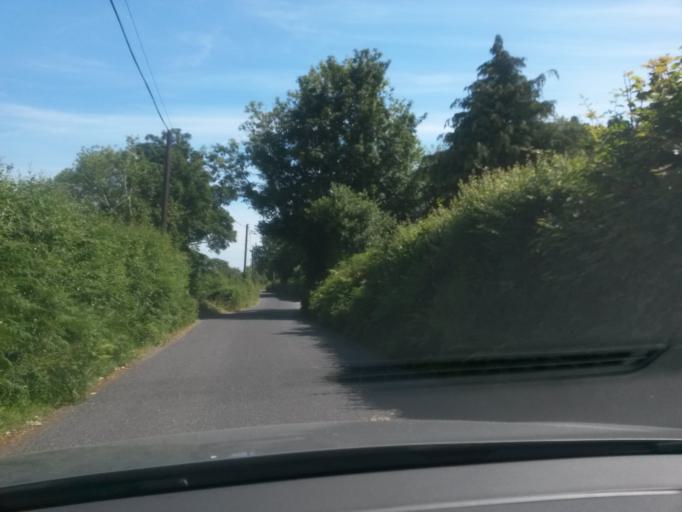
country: IE
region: Leinster
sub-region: Wicklow
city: Enniskerry
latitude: 53.1656
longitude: -6.1902
